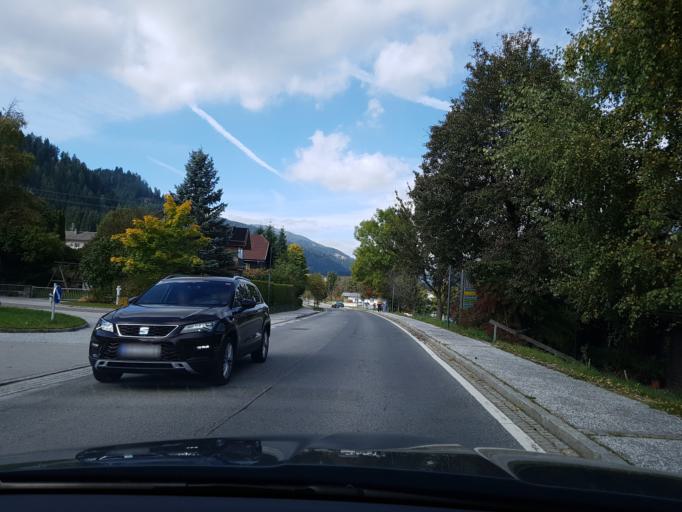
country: AT
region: Carinthia
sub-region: Politischer Bezirk Feldkirchen
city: Gnesau
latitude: 46.7756
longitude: 13.9625
